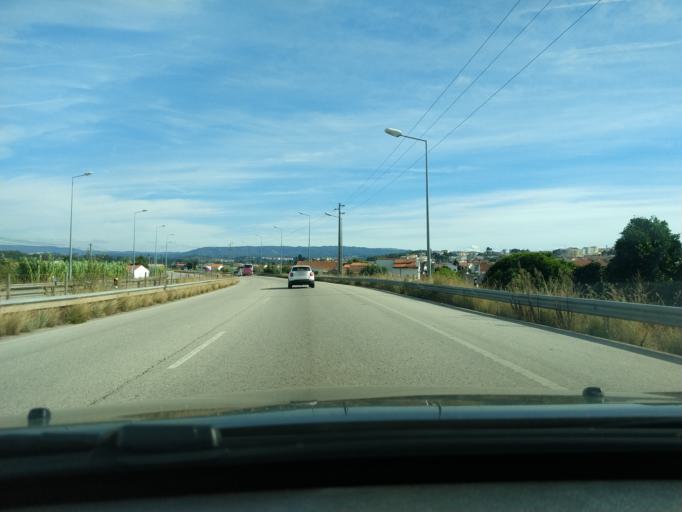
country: PT
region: Coimbra
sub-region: Coimbra
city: Coimbra
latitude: 40.2024
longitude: -8.4798
